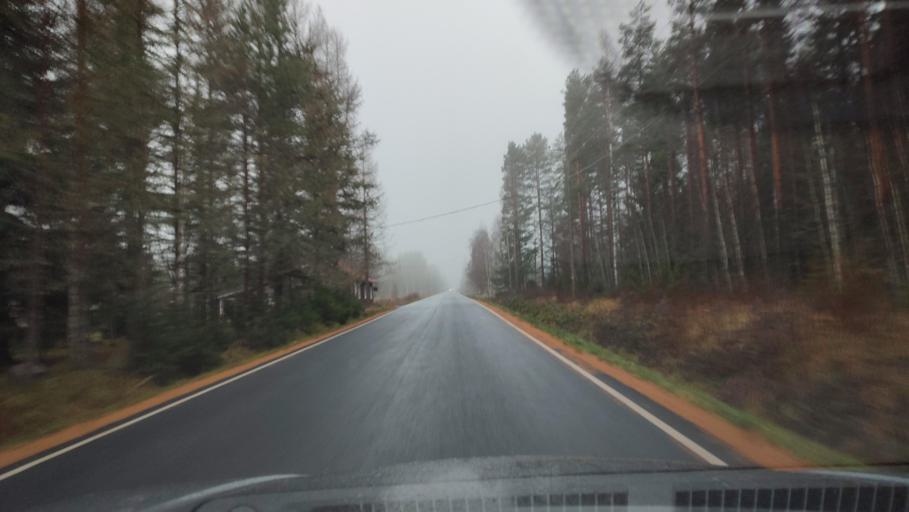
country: FI
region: Southern Ostrobothnia
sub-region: Suupohja
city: Karijoki
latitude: 62.1833
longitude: 21.7813
